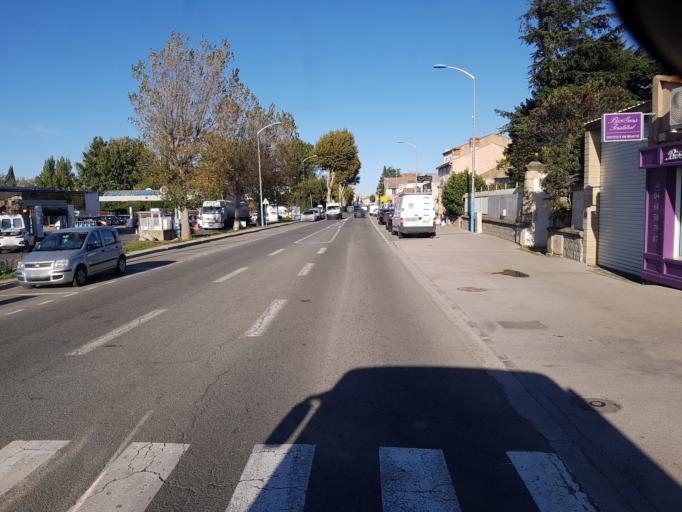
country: FR
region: Languedoc-Roussillon
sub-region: Departement de l'Aude
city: Coursan
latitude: 43.2289
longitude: 3.0512
